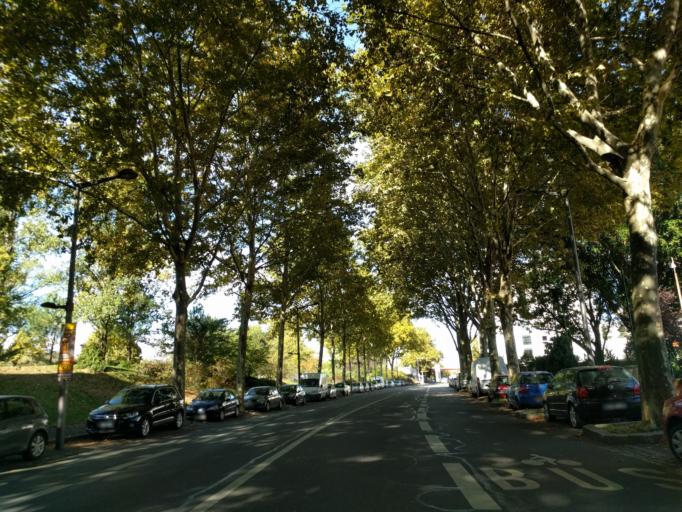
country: FR
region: Rhone-Alpes
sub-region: Departement du Rhone
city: La Mulatiere
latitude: 45.7353
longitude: 4.8237
